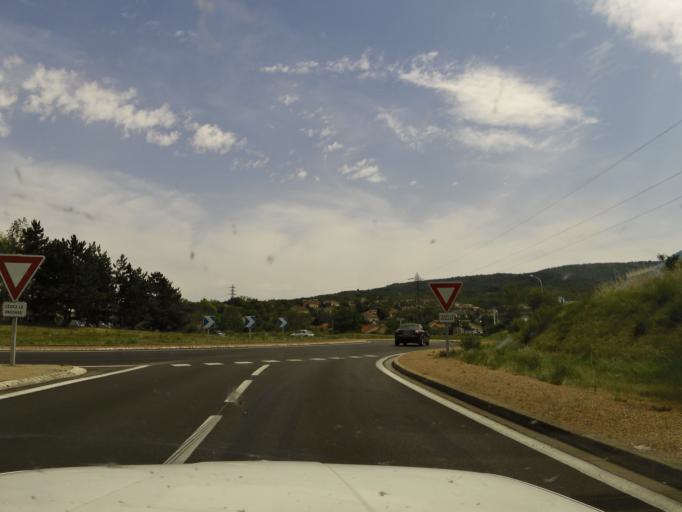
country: FR
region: Auvergne
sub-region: Departement du Puy-de-Dome
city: Aubiere
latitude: 45.7425
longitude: 3.1038
